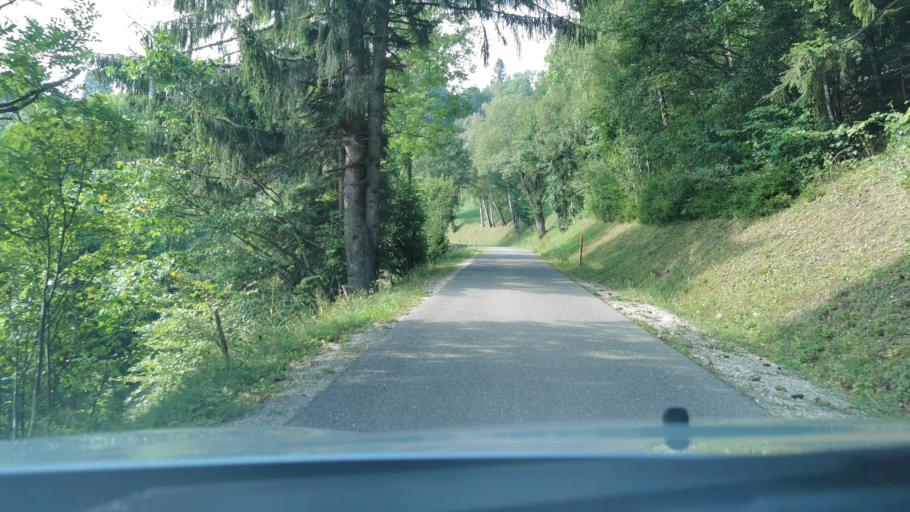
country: AT
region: Styria
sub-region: Politischer Bezirk Weiz
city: Fischbach
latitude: 47.3955
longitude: 15.6290
